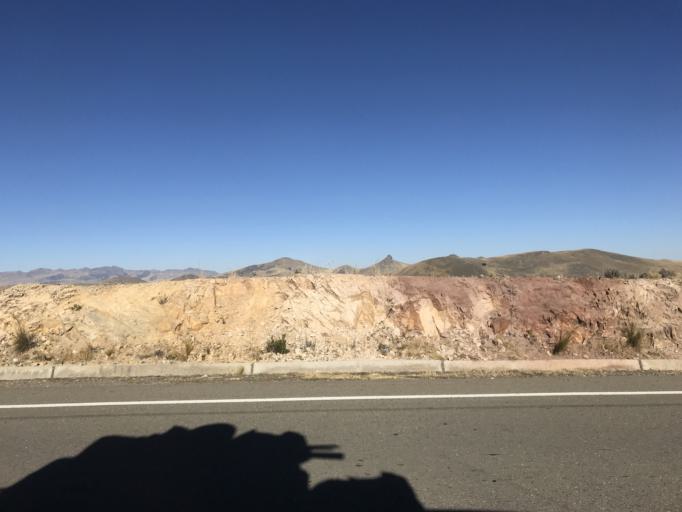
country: PE
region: Puno
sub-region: Yunguyo
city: Yunguyo
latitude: -16.1577
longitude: -68.9939
